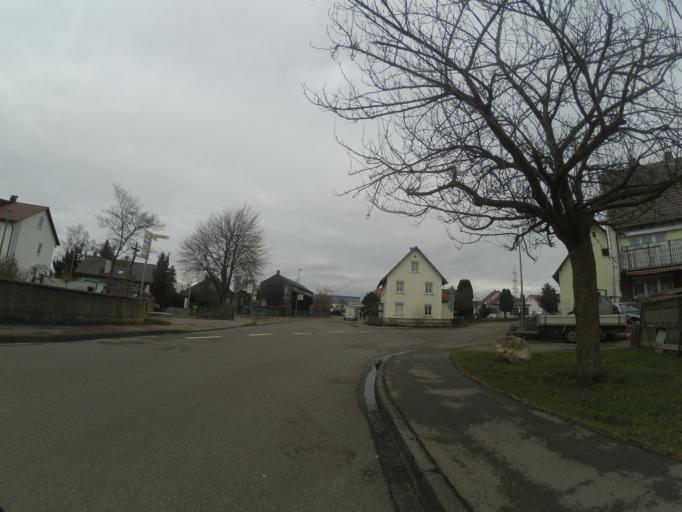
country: DE
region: Bavaria
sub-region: Swabia
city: Senden
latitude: 48.2990
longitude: 10.0543
